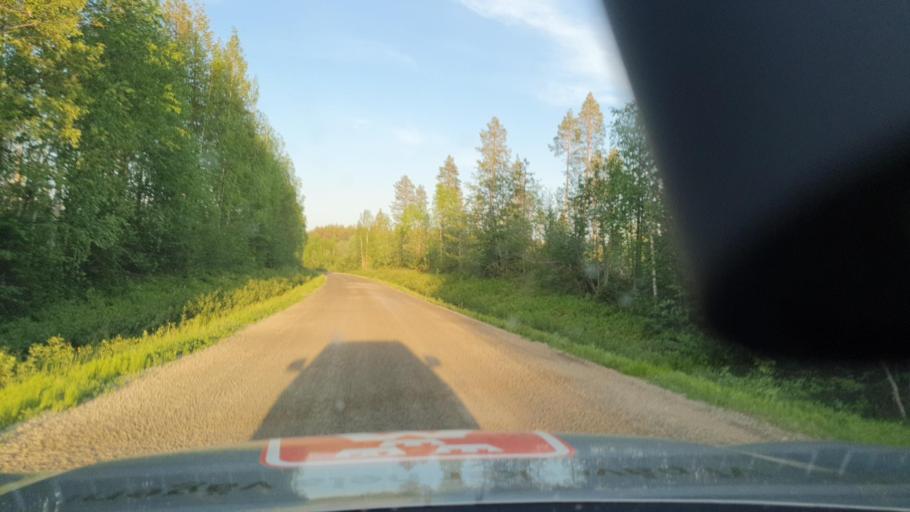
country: SE
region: Norrbotten
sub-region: Bodens Kommun
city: Boden
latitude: 66.1634
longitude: 21.5426
